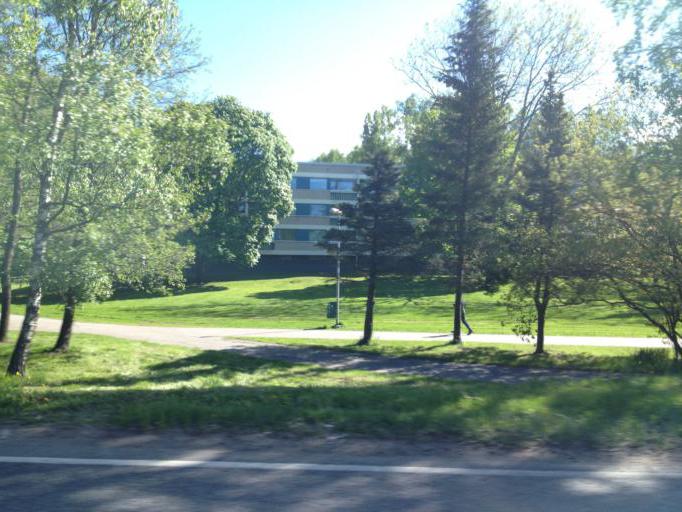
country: FI
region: Uusimaa
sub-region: Helsinki
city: Vantaa
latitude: 60.2178
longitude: 25.0837
